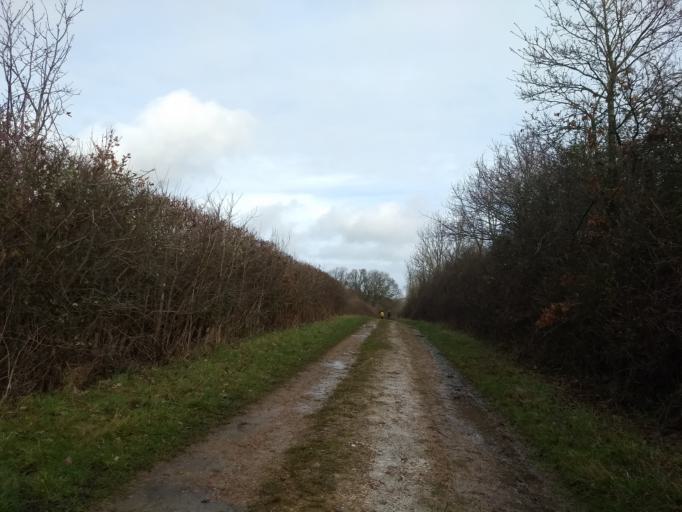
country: GB
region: England
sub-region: Isle of Wight
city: Newchurch
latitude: 50.7165
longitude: -1.2306
